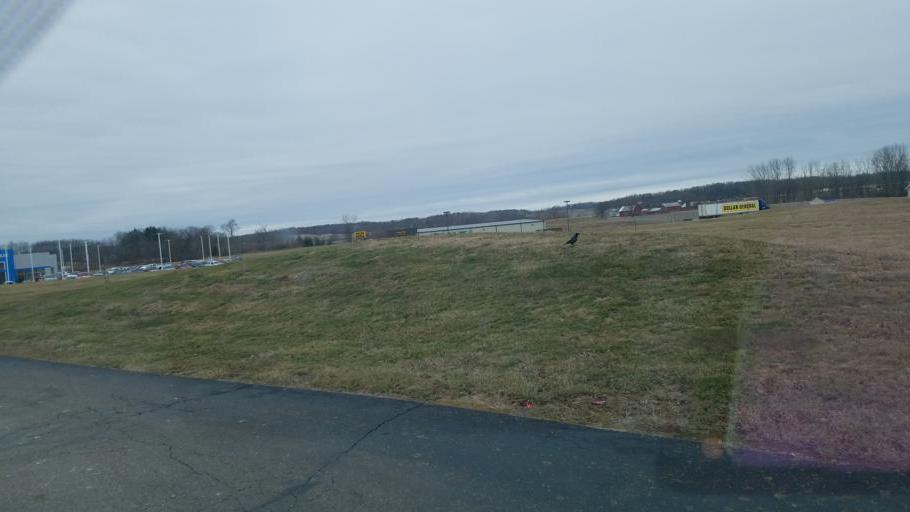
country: US
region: Ohio
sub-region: Knox County
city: Fredericktown
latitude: 40.4802
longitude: -82.5544
